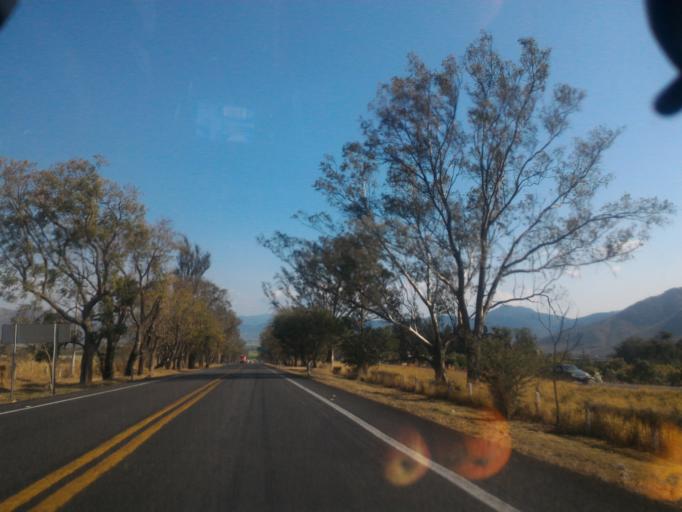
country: MX
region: Jalisco
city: Tuxpan
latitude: 19.5442
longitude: -103.4288
